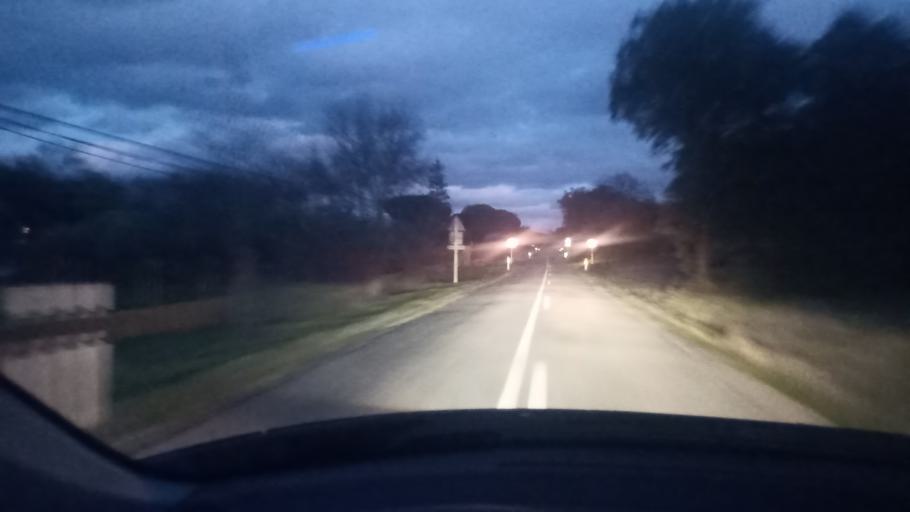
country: ES
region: Madrid
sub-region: Provincia de Madrid
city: Colmenar del Arroyo
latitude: 40.4301
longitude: -4.2138
